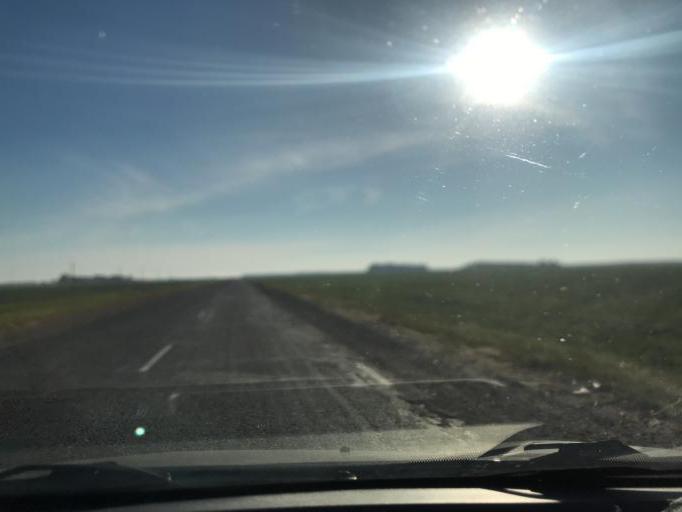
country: BY
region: Gomel
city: Brahin
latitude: 51.7951
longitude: 30.1548
